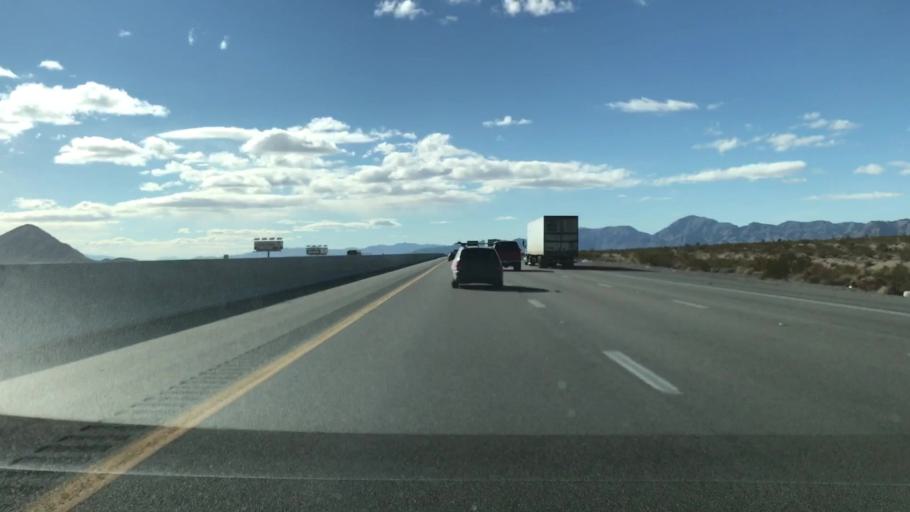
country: US
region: Nevada
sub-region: Clark County
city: Enterprise
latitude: 35.8205
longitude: -115.2994
